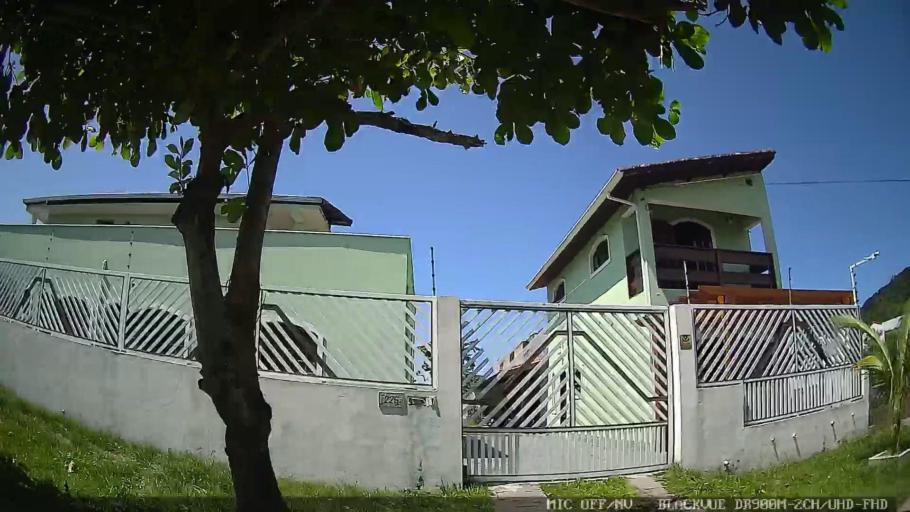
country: BR
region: Sao Paulo
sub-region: Peruibe
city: Peruibe
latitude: -24.3324
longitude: -47.0057
